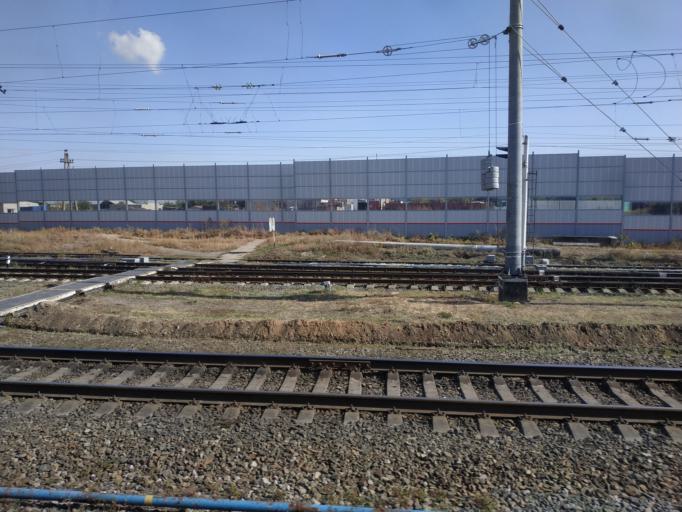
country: RU
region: Volgograd
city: Gumrak
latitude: 48.7778
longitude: 44.3795
